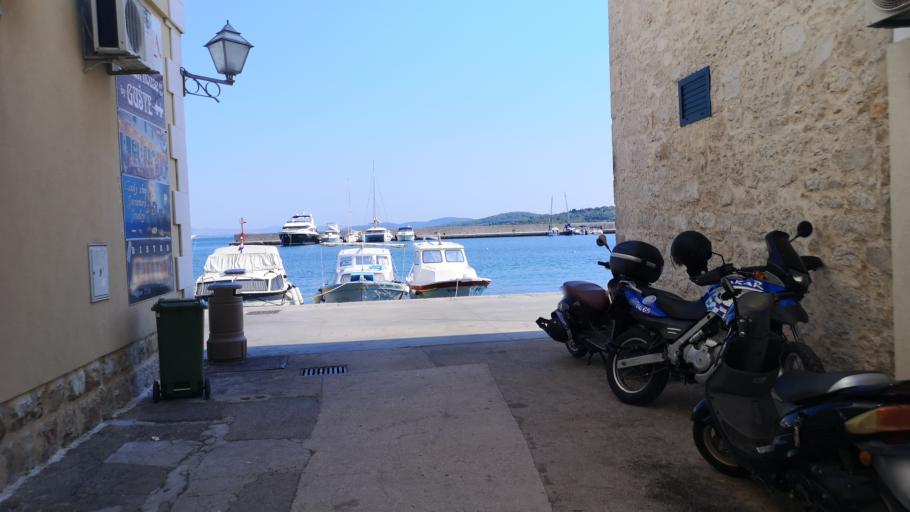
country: HR
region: Sibensko-Kniniska
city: Vodice
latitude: 43.7566
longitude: 15.7745
